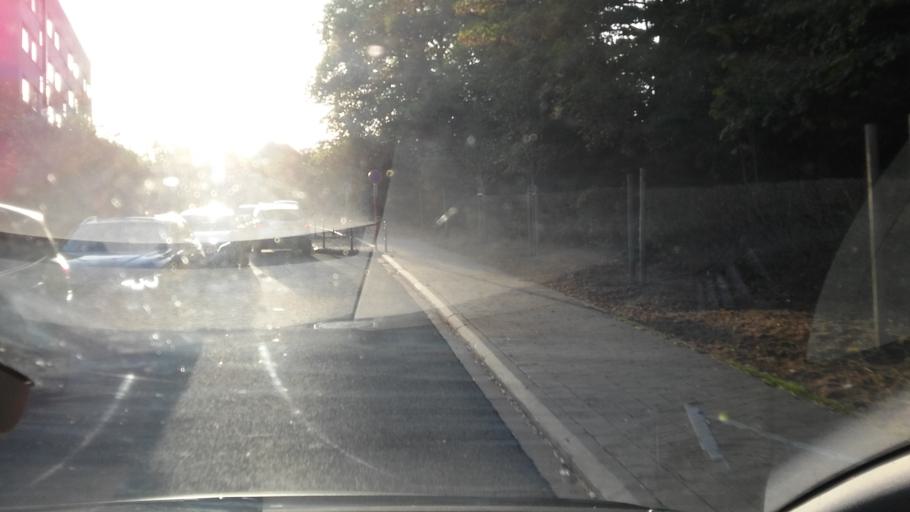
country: BE
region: Flanders
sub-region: Provincie Vlaams-Brabant
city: Hoeilaart
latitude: 50.8033
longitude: 4.4152
